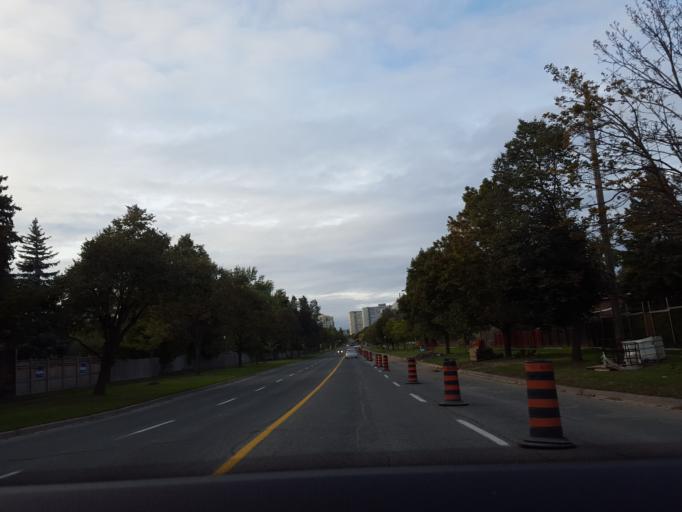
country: CA
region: Ontario
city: Scarborough
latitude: 43.7878
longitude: -79.3119
